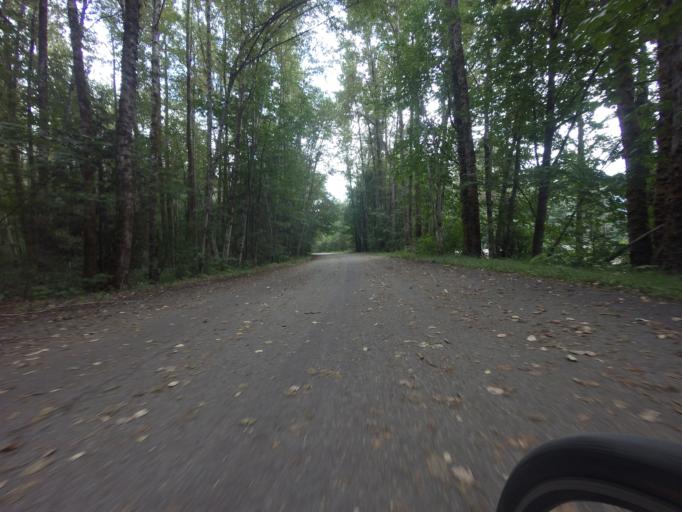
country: CA
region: British Columbia
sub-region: Greater Vancouver Regional District
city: Lions Bay
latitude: 49.7291
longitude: -123.1479
